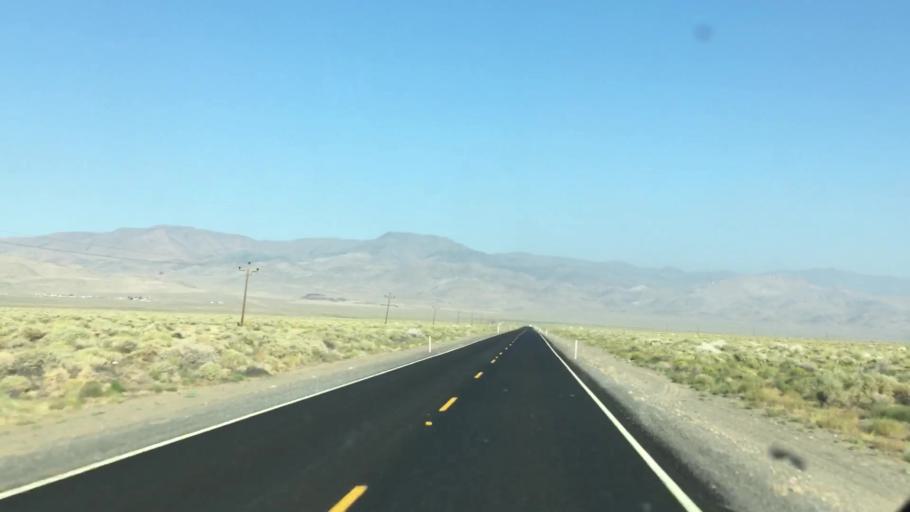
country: US
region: Nevada
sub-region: Lyon County
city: Fernley
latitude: 39.6457
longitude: -119.3114
